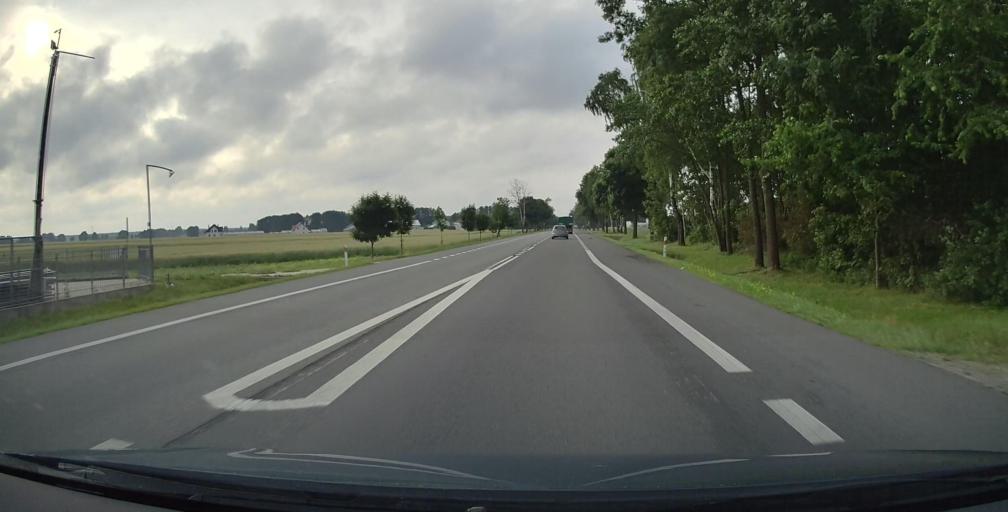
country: PL
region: Masovian Voivodeship
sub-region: Powiat siedlecki
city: Zbuczyn
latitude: 52.0956
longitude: 22.4168
